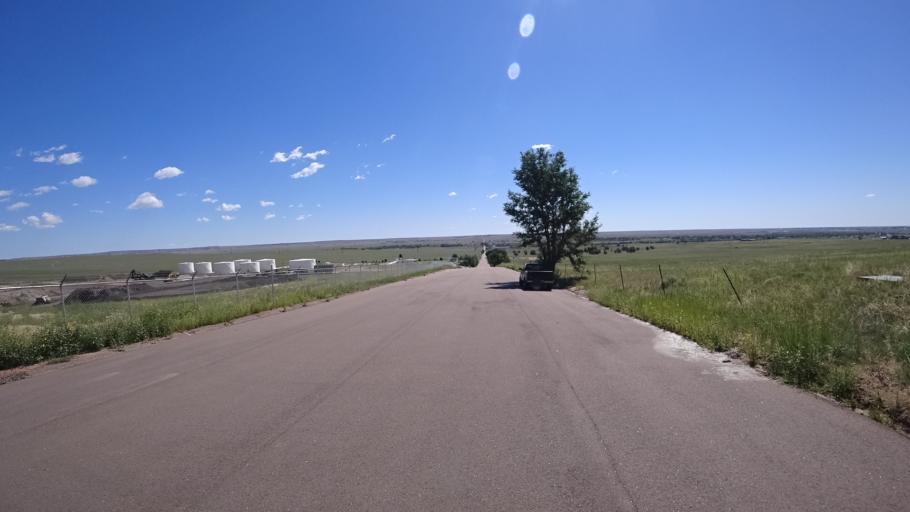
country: US
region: Colorado
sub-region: El Paso County
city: Security-Widefield
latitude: 38.7809
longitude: -104.6823
